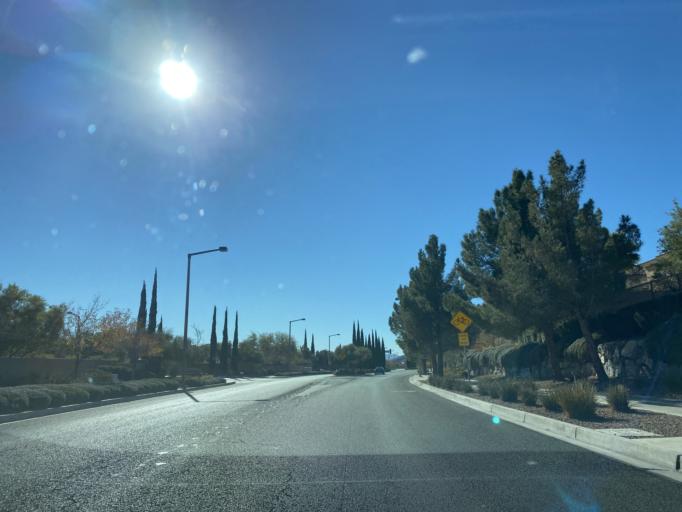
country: US
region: Nevada
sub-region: Clark County
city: Summerlin South
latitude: 36.1725
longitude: -115.3422
